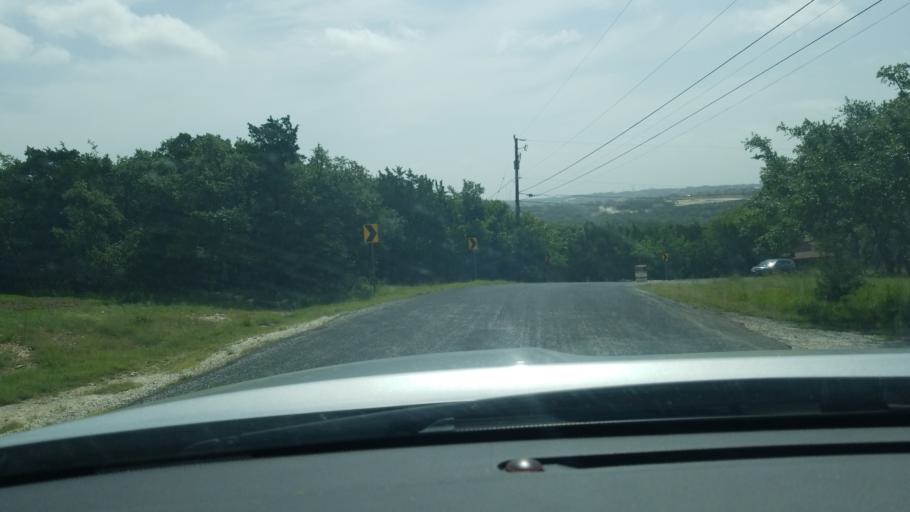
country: US
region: Texas
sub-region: Bexar County
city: Timberwood Park
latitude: 29.6859
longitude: -98.4925
